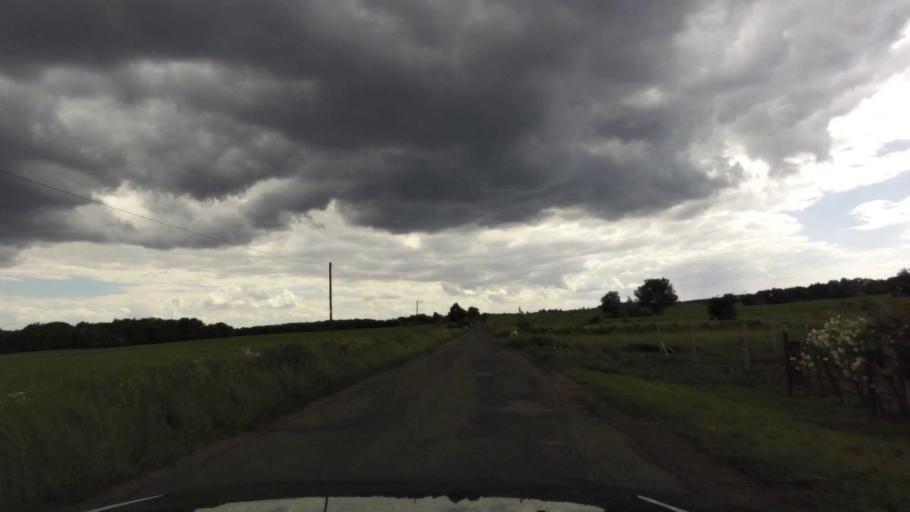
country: PL
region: West Pomeranian Voivodeship
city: Trzcinsko Zdroj
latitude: 52.9327
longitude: 14.5947
